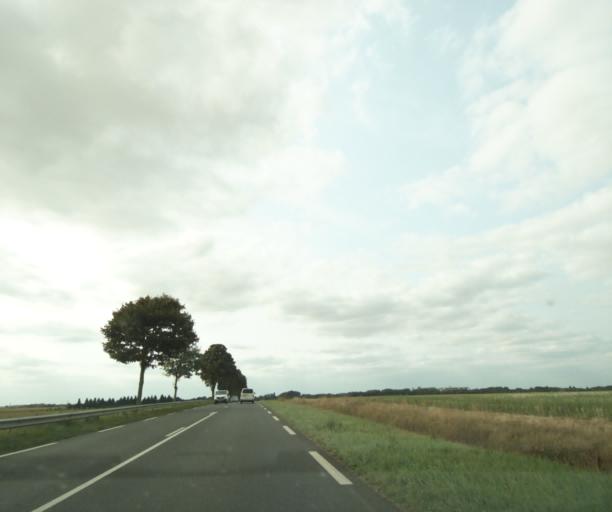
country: FR
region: Centre
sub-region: Departement d'Indre-et-Loire
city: Reignac-sur-Indre
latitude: 47.2018
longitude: 0.9116
